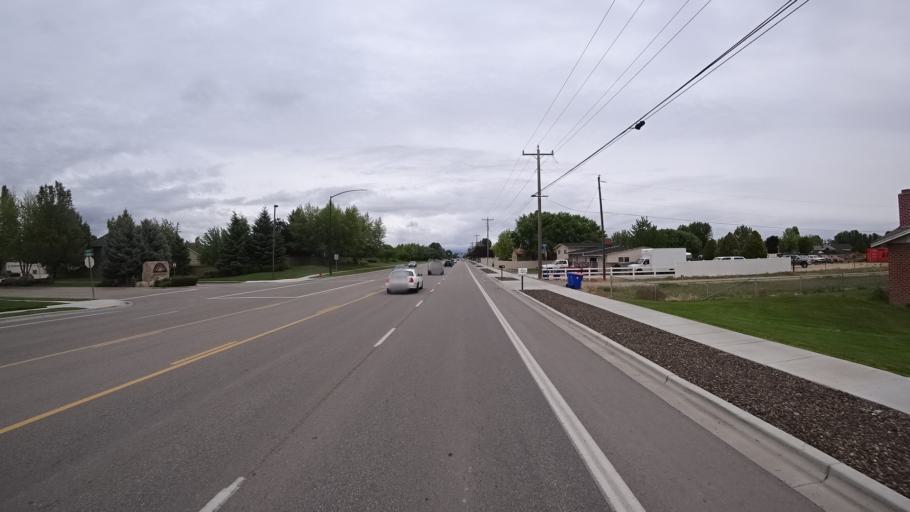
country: US
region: Idaho
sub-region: Ada County
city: Meridian
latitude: 43.6338
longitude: -116.3910
